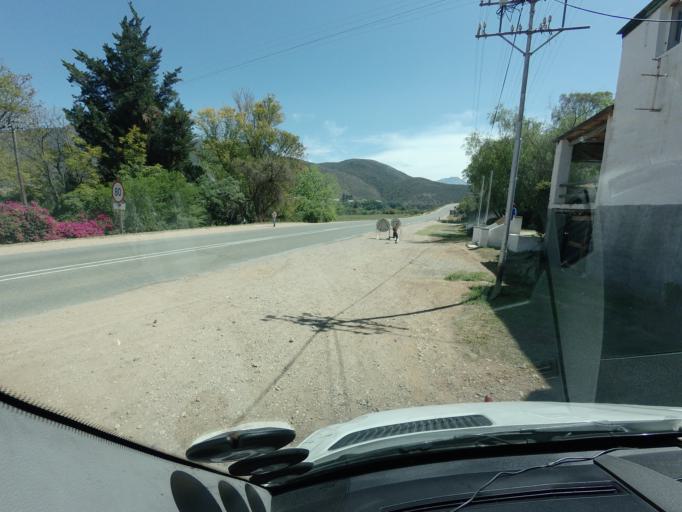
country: ZA
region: Western Cape
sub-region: Eden District Municipality
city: Oudtshoorn
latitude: -33.4812
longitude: 22.2477
